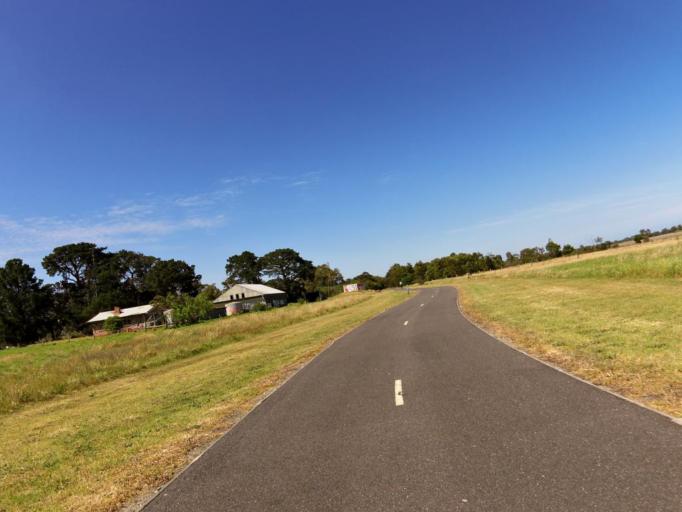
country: AU
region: Victoria
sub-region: Kingston
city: Carrum
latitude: -38.0868
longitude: 145.1460
